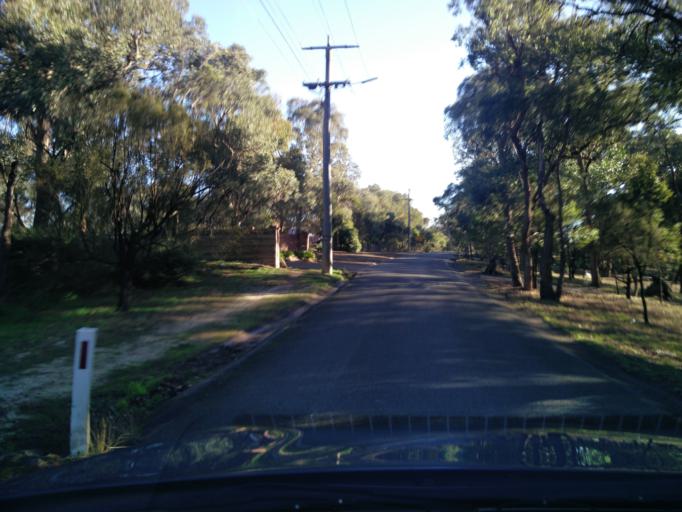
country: AU
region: Victoria
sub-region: Nillumbik
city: Research
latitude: -37.7109
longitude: 145.1774
